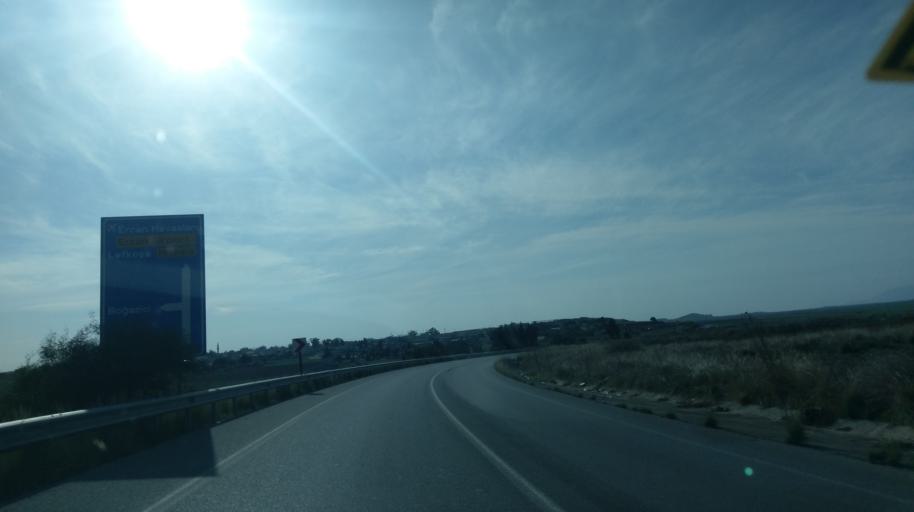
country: CY
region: Ammochostos
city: Trikomo
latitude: 35.2758
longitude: 33.8321
